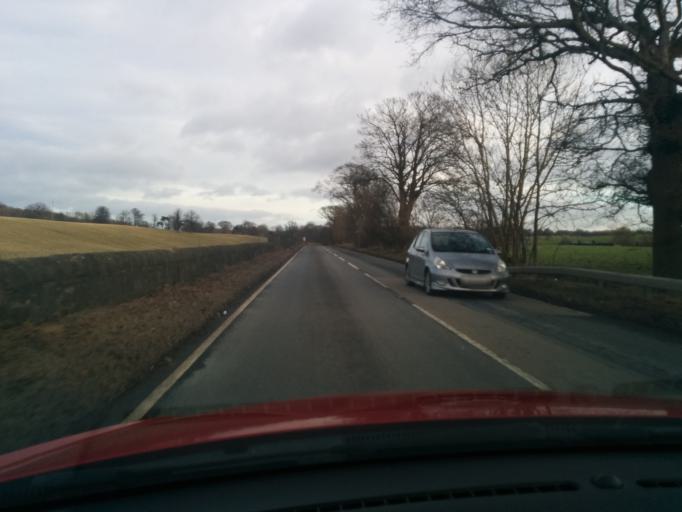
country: GB
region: Scotland
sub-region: Fife
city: Limekilns
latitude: 55.9844
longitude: -3.5218
